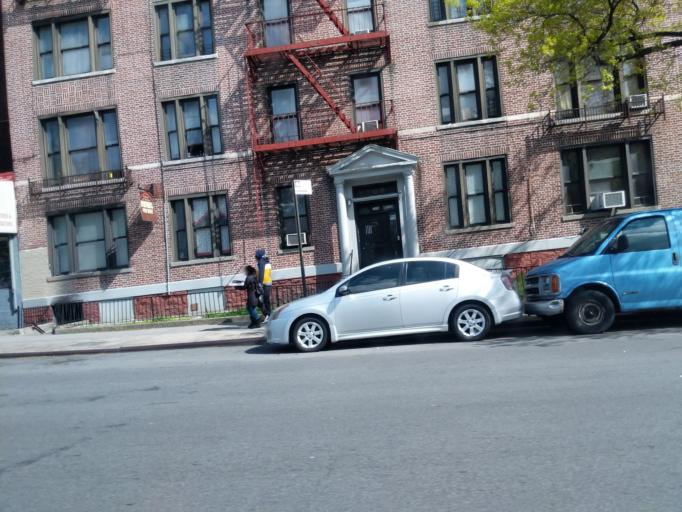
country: US
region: New York
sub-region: New York County
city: Inwood
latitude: 40.8624
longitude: -73.9100
